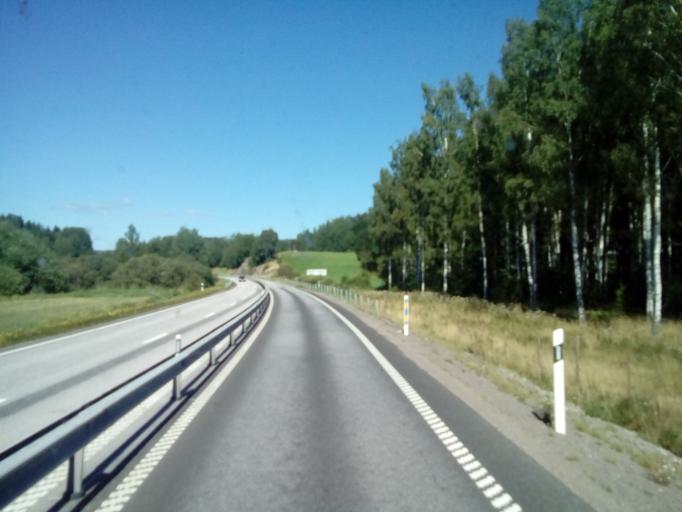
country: SE
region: OEstergoetland
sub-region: Kinda Kommun
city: Kisa
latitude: 58.0504
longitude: 15.6657
